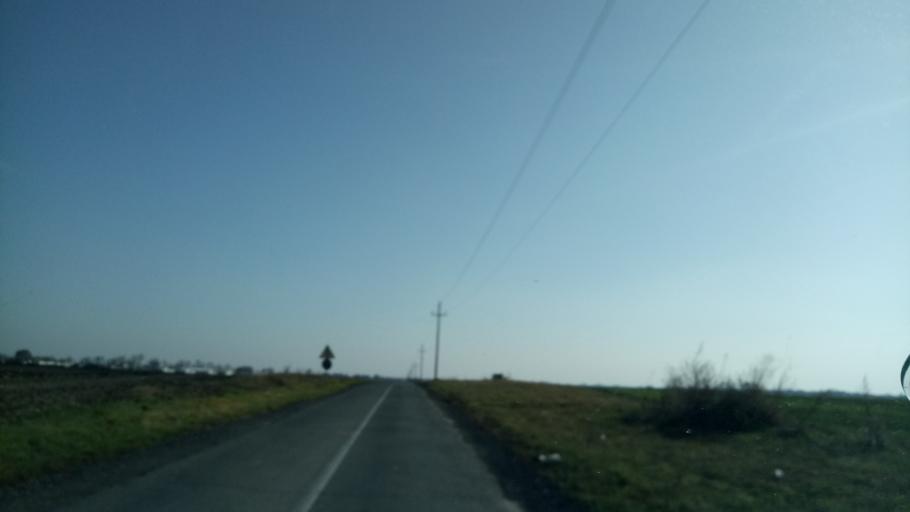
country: RS
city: Ljukovo
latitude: 45.0441
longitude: 20.0340
